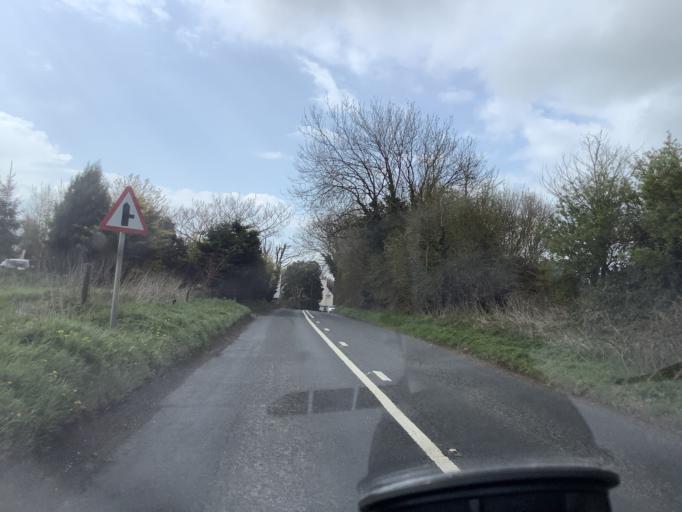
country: GB
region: England
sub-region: Borough of Swindon
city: Wroughton
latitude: 51.4886
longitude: -1.8398
